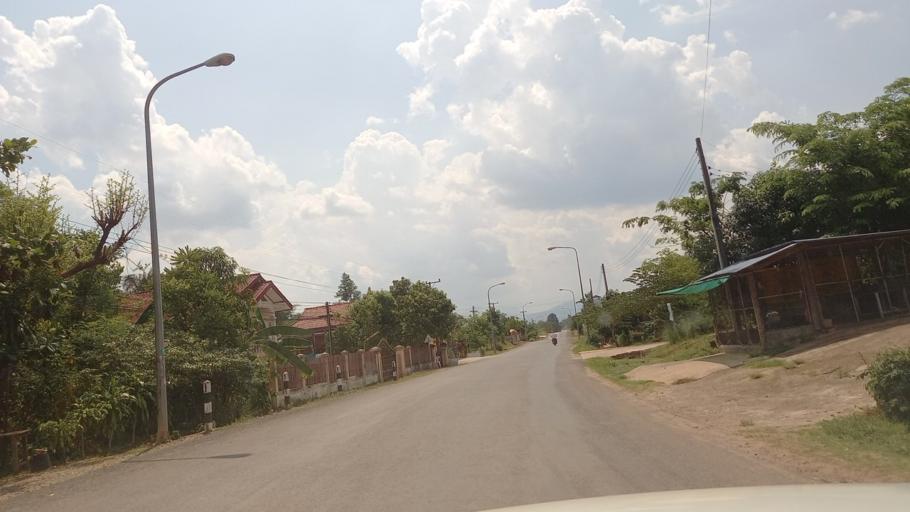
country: LA
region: Bolikhamxai
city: Muang Pakxan
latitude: 18.4175
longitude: 103.6379
